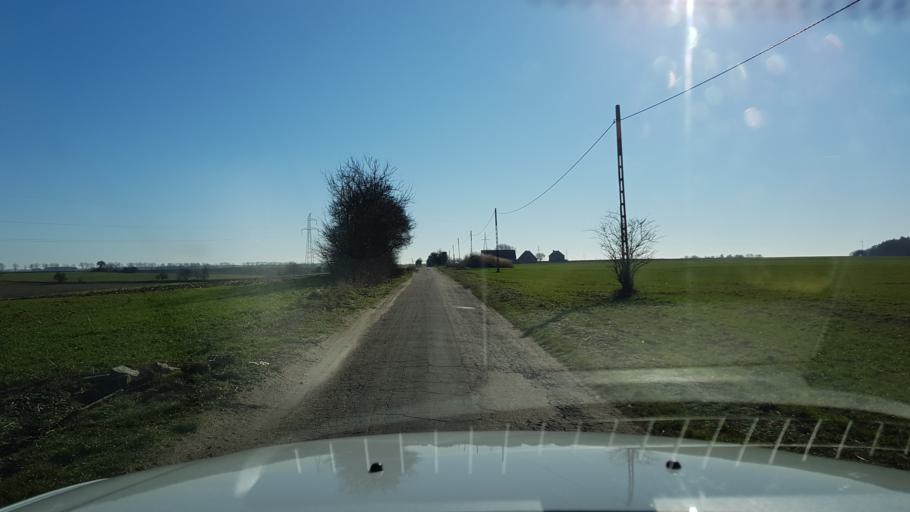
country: PL
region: West Pomeranian Voivodeship
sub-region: Powiat pyrzycki
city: Przelewice
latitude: 53.0495
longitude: 15.0593
